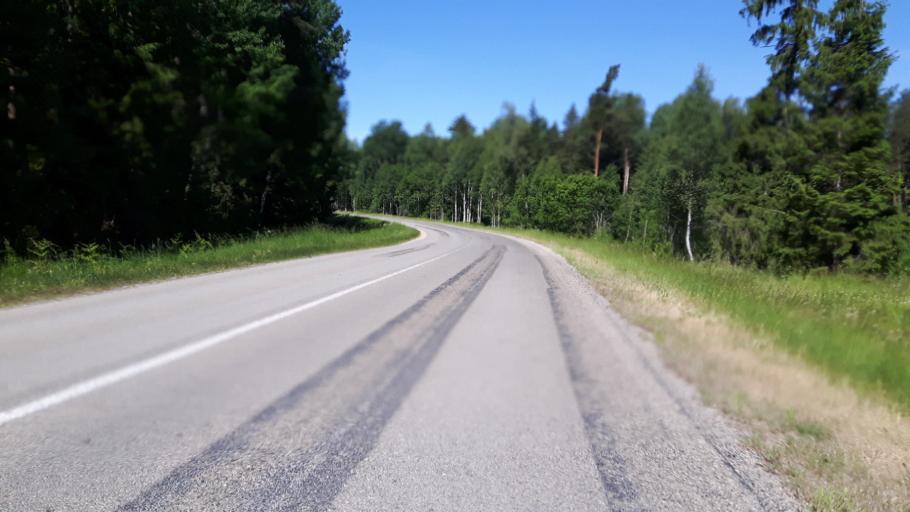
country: LV
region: Tukuma Rajons
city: Tukums
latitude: 57.0159
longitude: 23.0448
